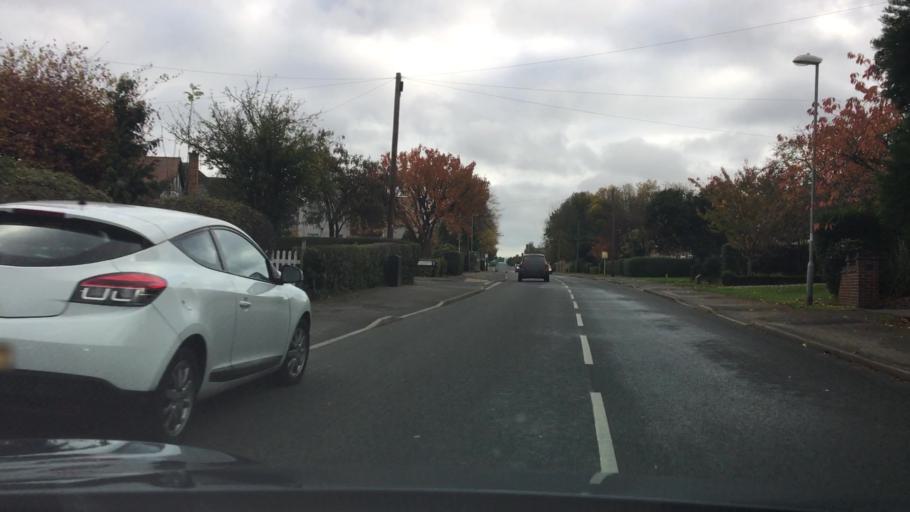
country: GB
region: England
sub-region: Nottinghamshire
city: Radcliffe on Trent
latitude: 52.9481
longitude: -1.0287
